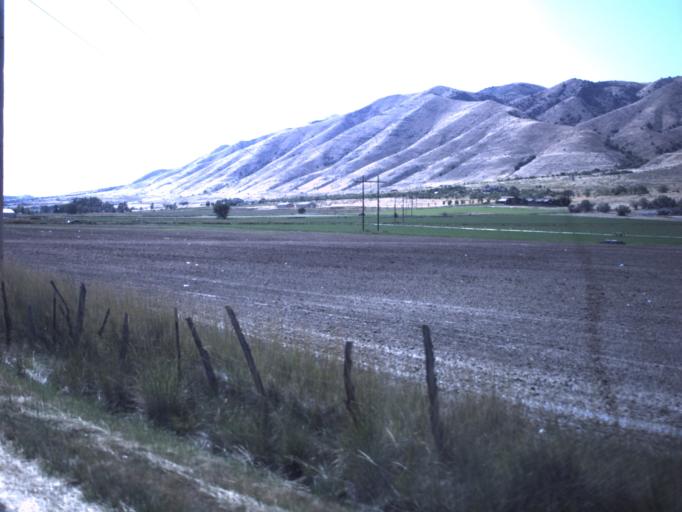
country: US
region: Utah
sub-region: Utah County
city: West Mountain
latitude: 40.0969
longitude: -111.7882
